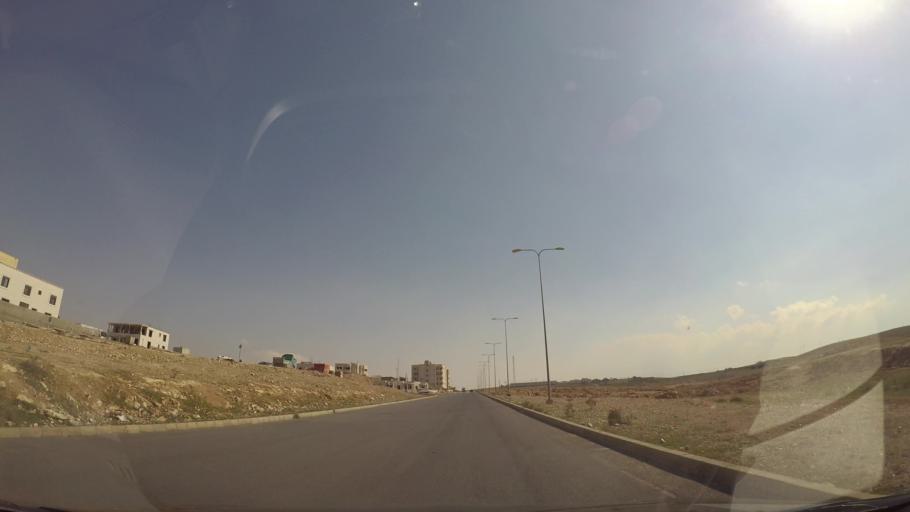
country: JO
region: Zarqa
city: Zarqa
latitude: 32.0503
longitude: 36.1153
